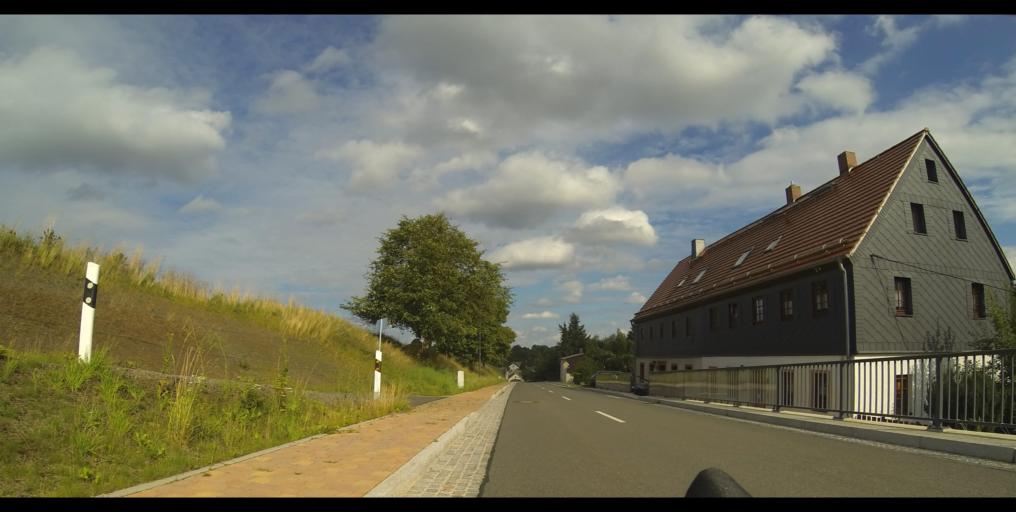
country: DE
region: Saxony
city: Hainichen
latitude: 50.9887
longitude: 13.1717
